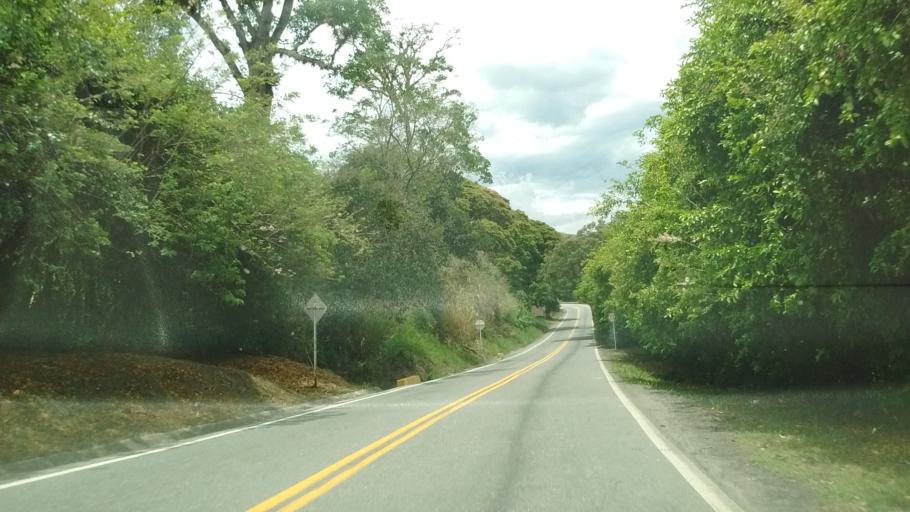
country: CO
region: Cauca
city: La Sierra
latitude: 2.2063
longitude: -76.8091
